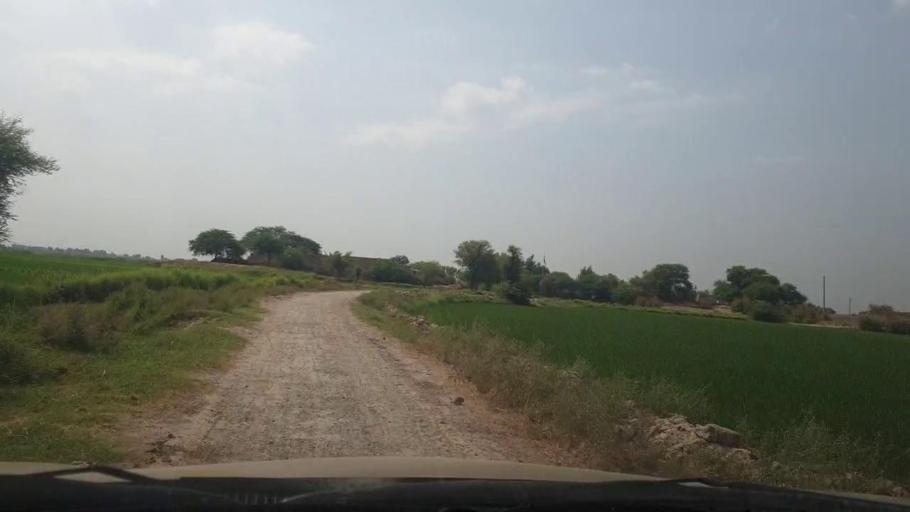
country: PK
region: Sindh
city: Larkana
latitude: 27.6820
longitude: 68.2025
